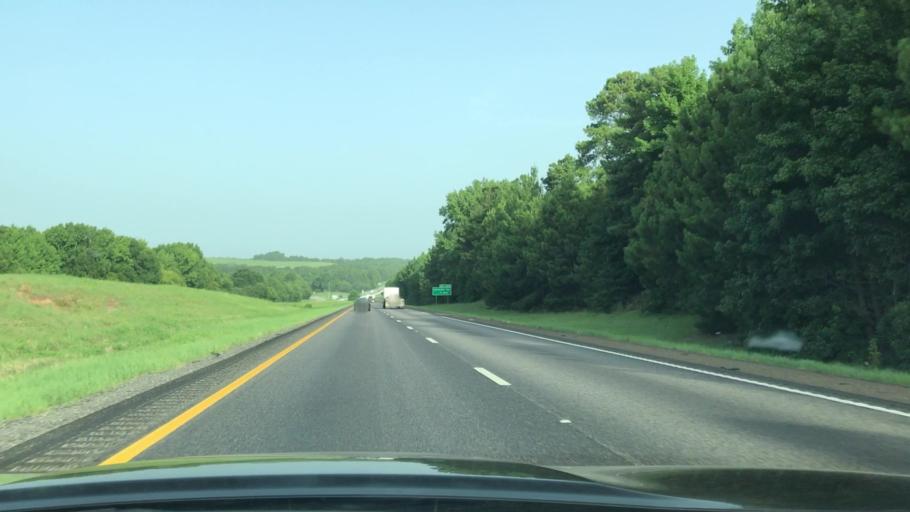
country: US
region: Texas
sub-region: Smith County
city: Tyler
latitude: 32.4557
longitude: -95.2983
